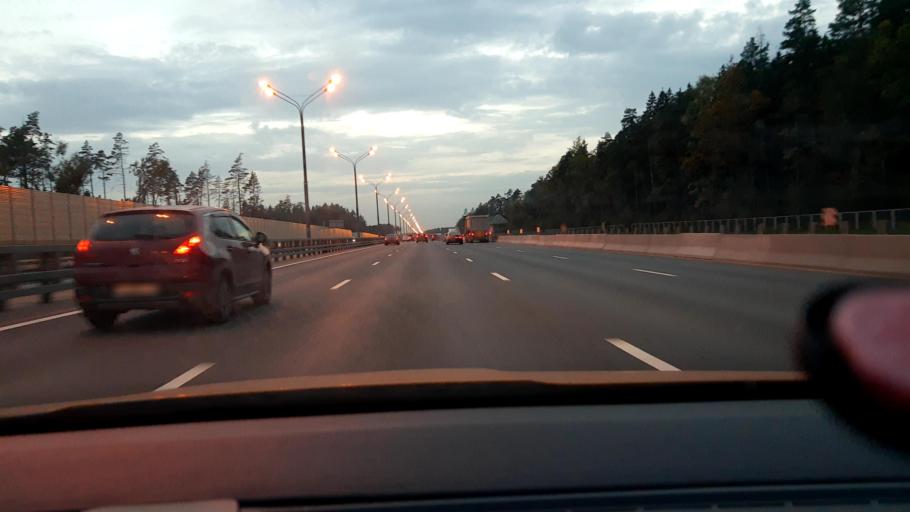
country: RU
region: Moskovskaya
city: Zhavoronki
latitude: 55.6198
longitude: 37.1189
